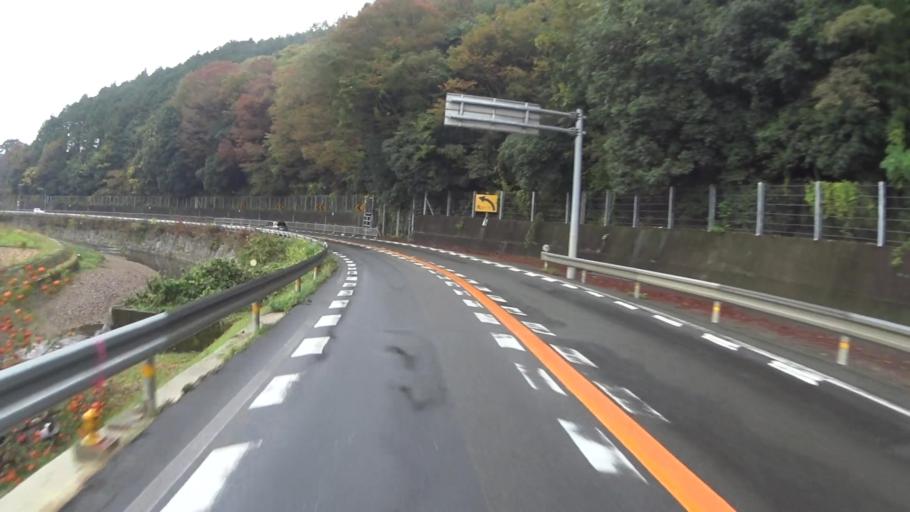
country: JP
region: Kyoto
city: Ayabe
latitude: 35.1900
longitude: 135.3102
